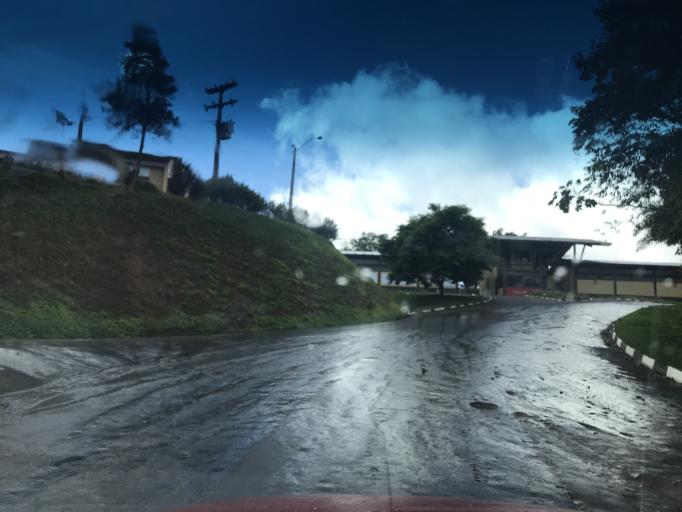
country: BR
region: Bahia
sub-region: Gandu
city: Gandu
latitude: -13.8990
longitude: -39.4597
